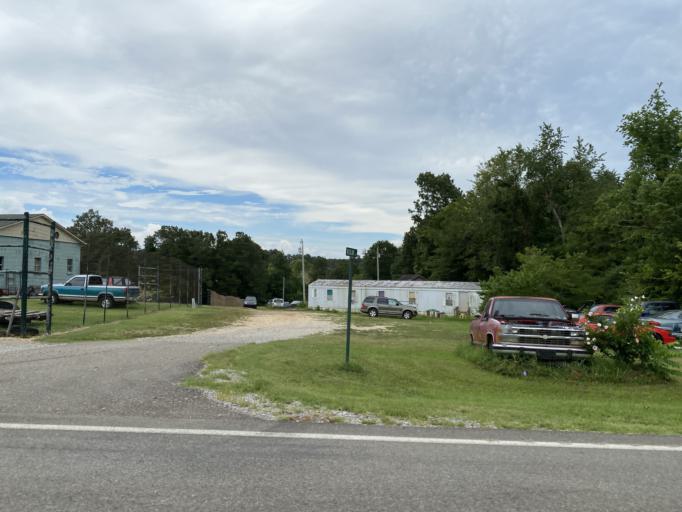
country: US
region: Arkansas
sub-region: Fulton County
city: Salem
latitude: 36.3645
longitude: -91.8285
